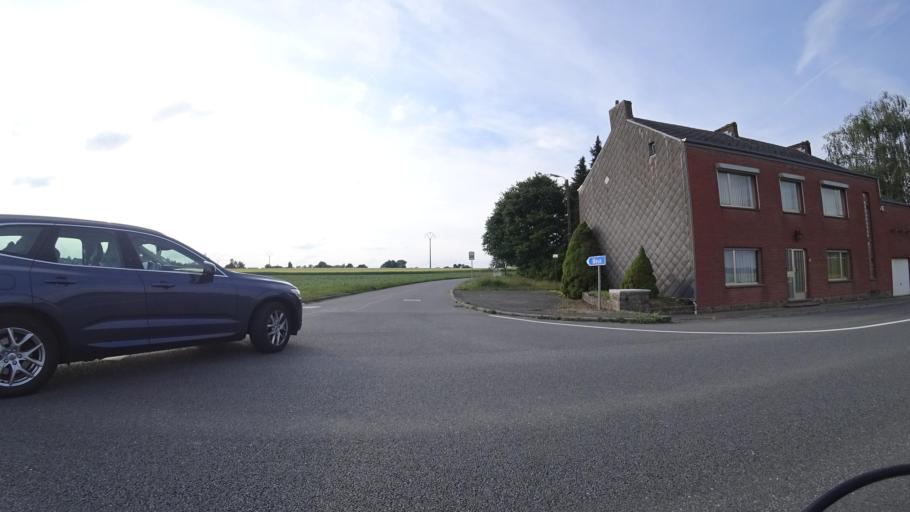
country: BE
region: Wallonia
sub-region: Province du Brabant Wallon
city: Perwez
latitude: 50.5412
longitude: 4.7924
